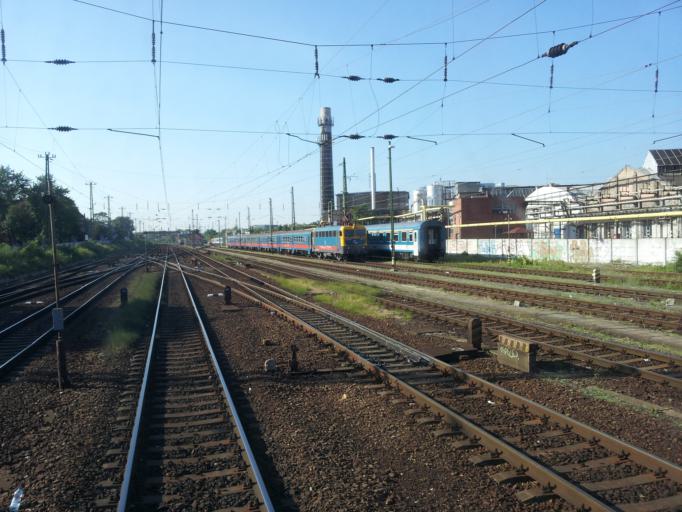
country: HU
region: Budapest
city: Budapest XIV. keruelet
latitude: 47.4973
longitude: 19.0994
